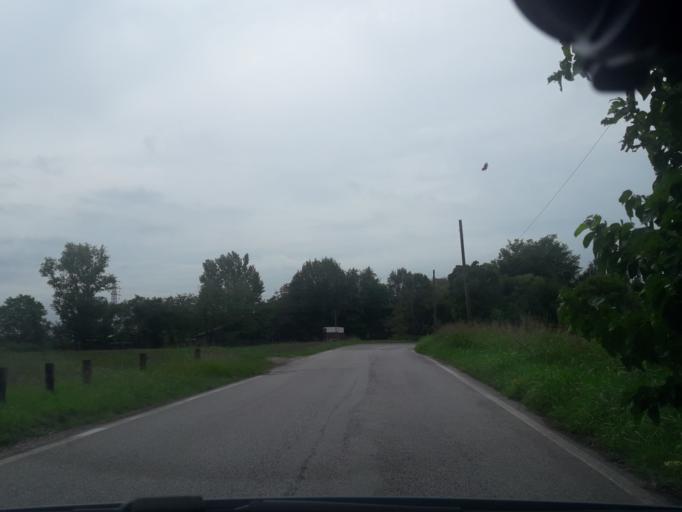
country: IT
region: Friuli Venezia Giulia
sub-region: Provincia di Udine
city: Udine
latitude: 46.0686
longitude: 13.2826
